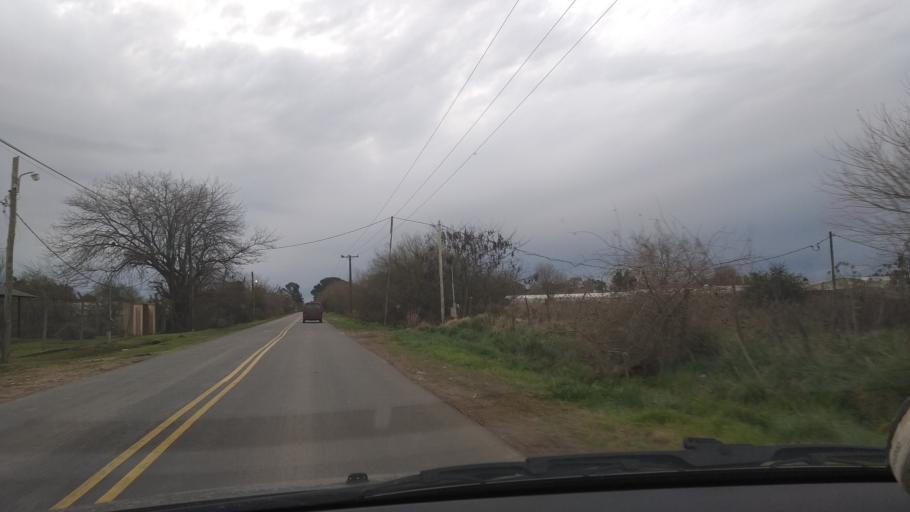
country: AR
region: Buenos Aires
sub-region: Partido de La Plata
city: La Plata
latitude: -35.0033
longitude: -58.0634
